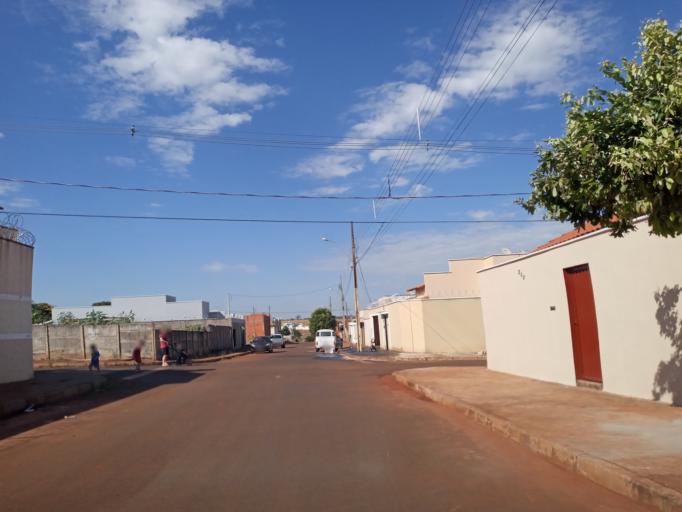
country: BR
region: Minas Gerais
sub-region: Ituiutaba
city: Ituiutaba
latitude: -18.9939
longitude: -49.4648
